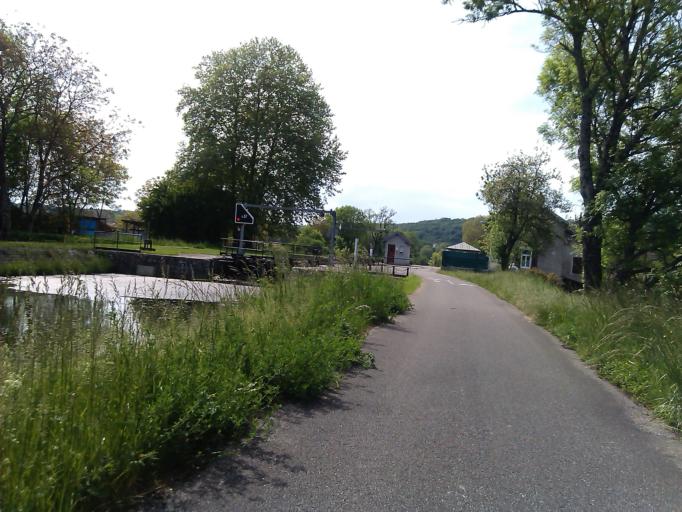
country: FR
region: Franche-Comte
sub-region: Departement du Doubs
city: Quingey
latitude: 47.1392
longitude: 5.8598
